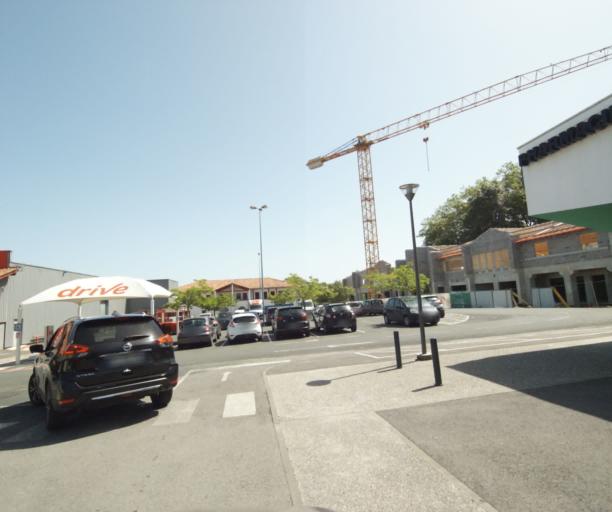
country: FR
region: Aquitaine
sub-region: Departement des Pyrenees-Atlantiques
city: Bayonne
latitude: 43.4766
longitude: -1.4566
